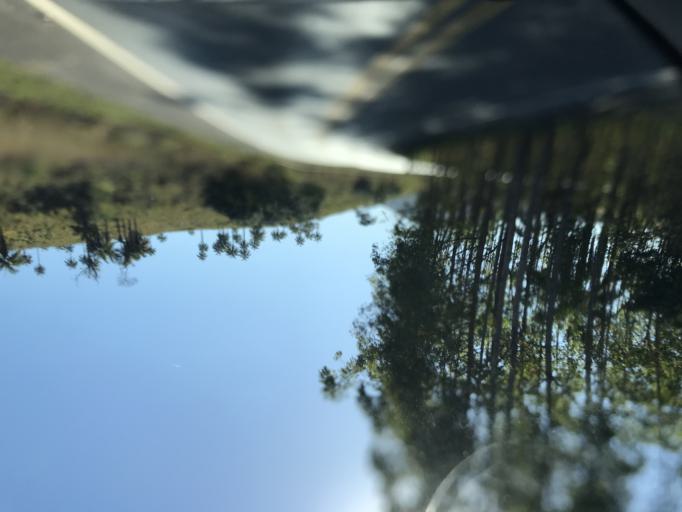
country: BR
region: Minas Gerais
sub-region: Bambui
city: Bambui
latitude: -19.8188
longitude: -46.0200
